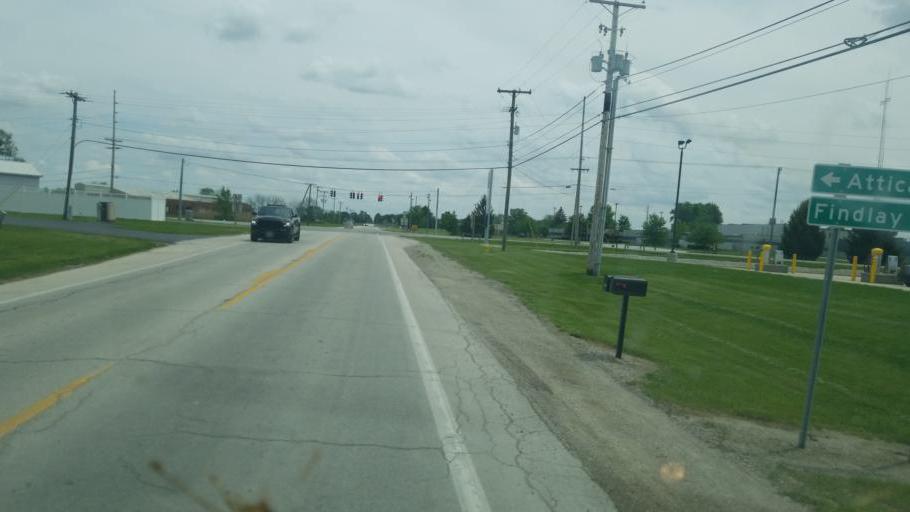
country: US
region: Ohio
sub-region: Seneca County
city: Tiffin
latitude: 41.0816
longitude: -83.1539
